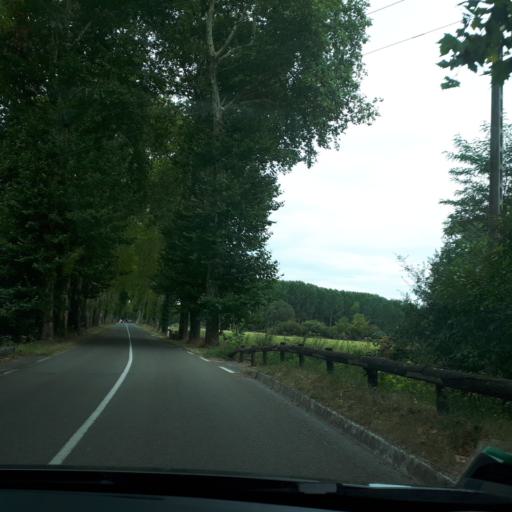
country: FR
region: Centre
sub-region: Departement du Loiret
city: Poilly-lez-Gien
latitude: 47.6809
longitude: 2.6096
